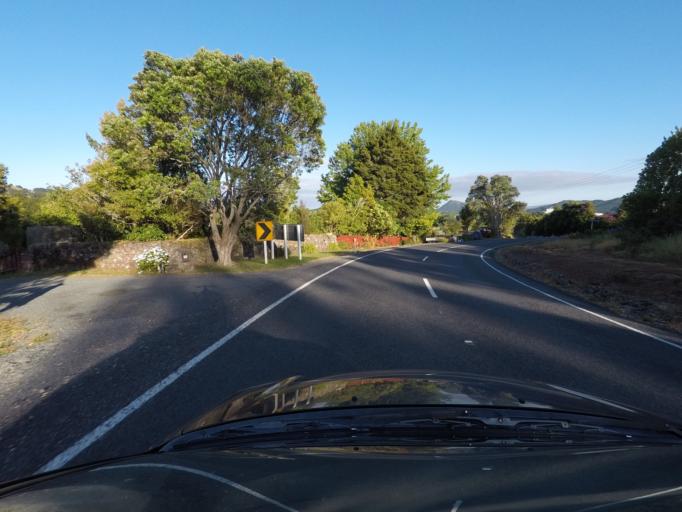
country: NZ
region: Northland
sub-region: Whangarei
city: Whangarei
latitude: -35.6525
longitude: 174.3063
